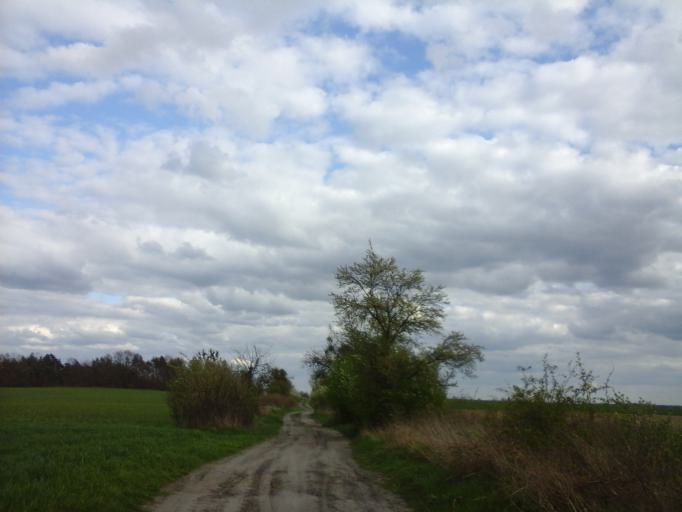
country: PL
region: West Pomeranian Voivodeship
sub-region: Powiat choszczenski
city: Krzecin
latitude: 53.1016
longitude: 15.5198
